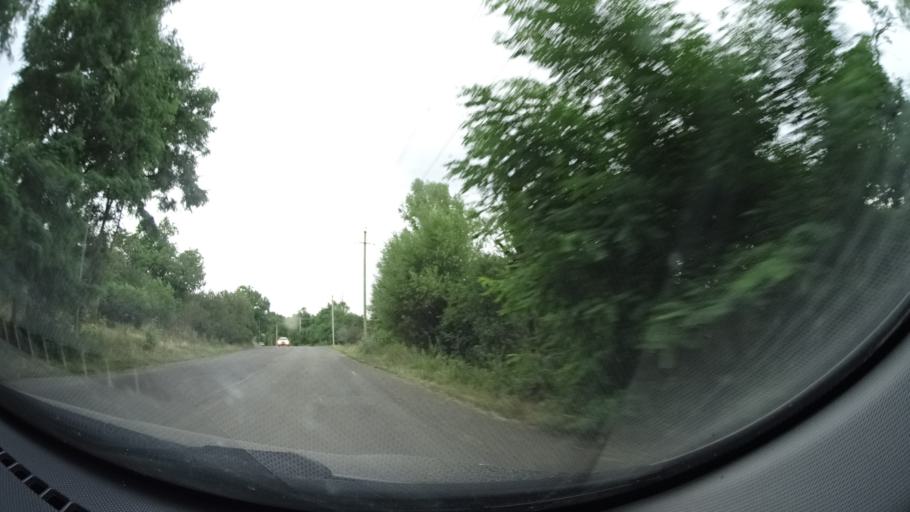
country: GE
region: Samtskhe-Javakheti
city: Akhaltsikhe
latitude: 41.6301
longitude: 43.0470
